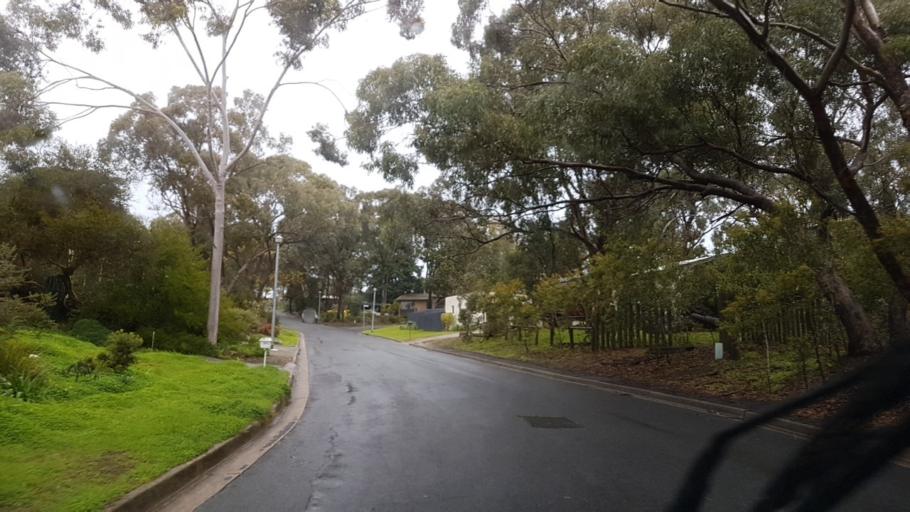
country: AU
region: South Australia
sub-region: Onkaparinga
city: Bedford Park
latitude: -35.0457
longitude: 138.5858
